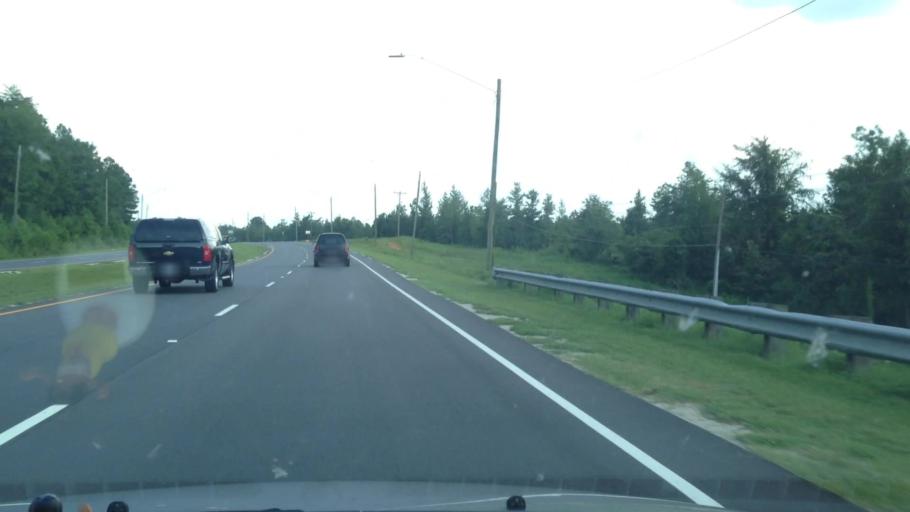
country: US
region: North Carolina
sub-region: Harnett County
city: Lillington
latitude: 35.4131
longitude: -78.7945
